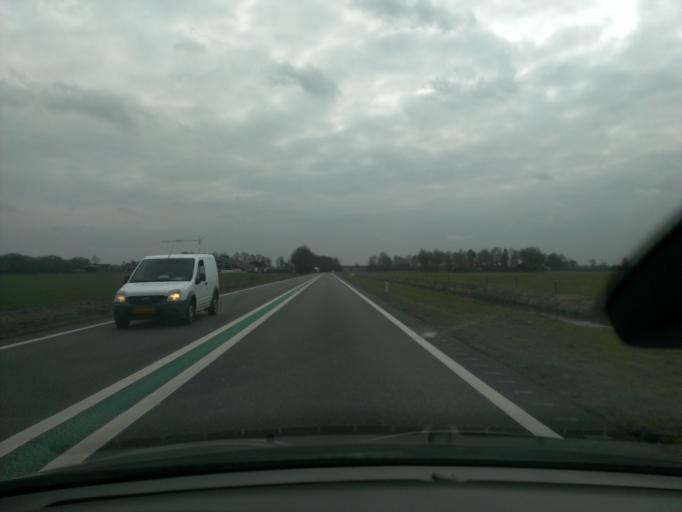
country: NL
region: Overijssel
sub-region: Gemeente Twenterand
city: Den Ham
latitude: 52.5708
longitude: 6.4200
